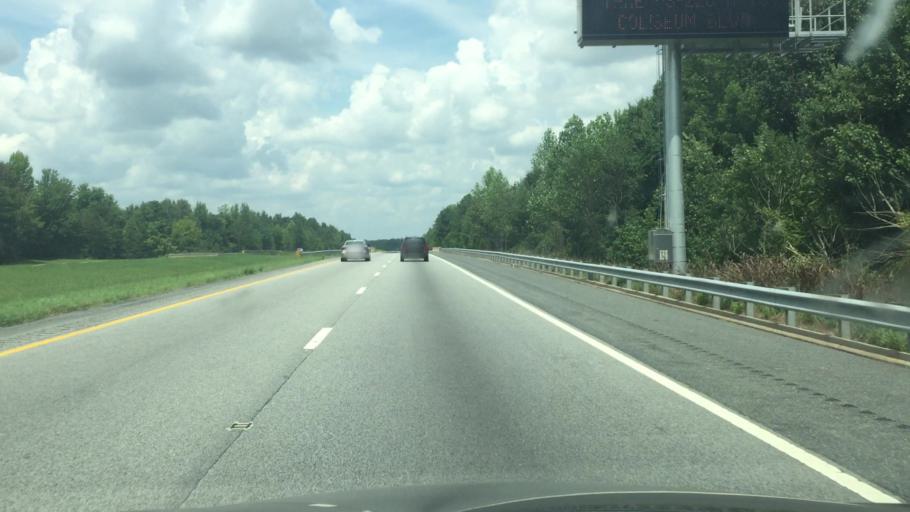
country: US
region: North Carolina
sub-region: Guilford County
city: Pleasant Garden
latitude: 35.9650
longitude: -79.8205
